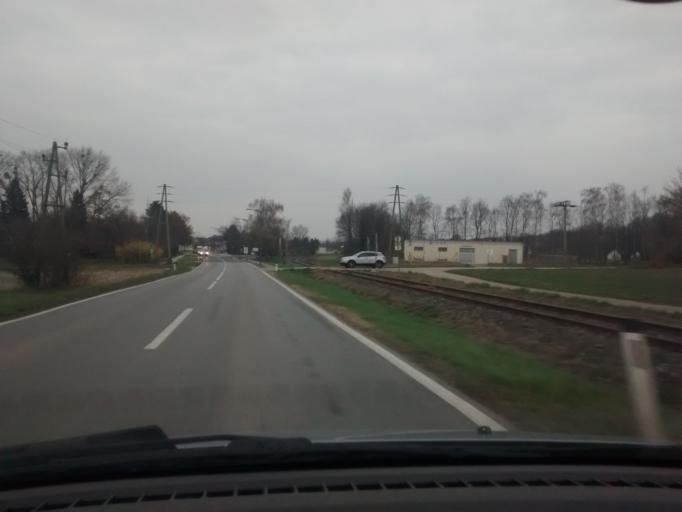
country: AT
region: Lower Austria
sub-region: Politischer Bezirk Bruck an der Leitha
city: Enzersdorf an der Fischa
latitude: 48.0984
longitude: 16.6057
